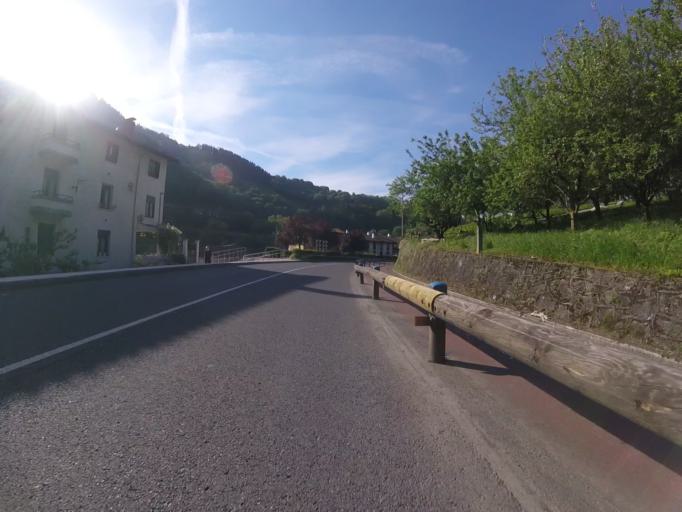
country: ES
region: Basque Country
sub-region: Provincia de Guipuzcoa
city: Isasondo
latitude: 43.0715
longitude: -2.1627
